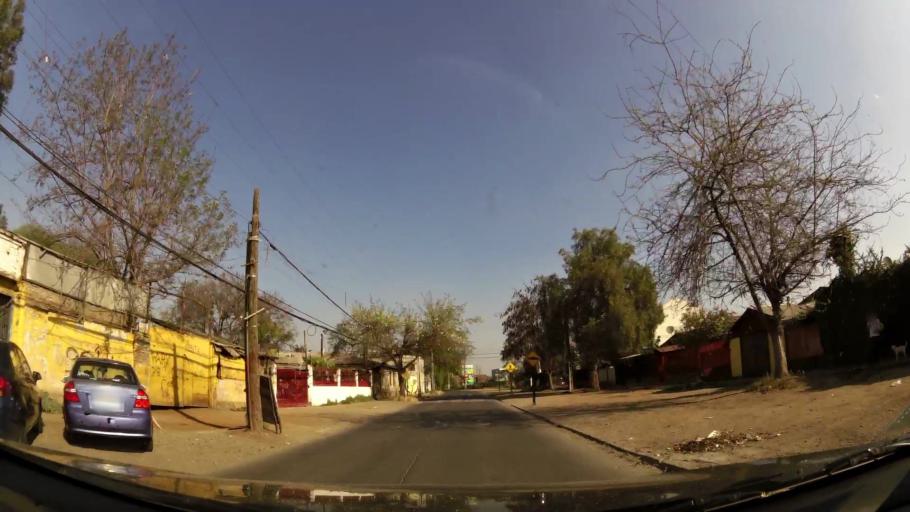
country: CL
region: Santiago Metropolitan
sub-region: Provincia de Santiago
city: Santiago
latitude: -33.3937
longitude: -70.6763
